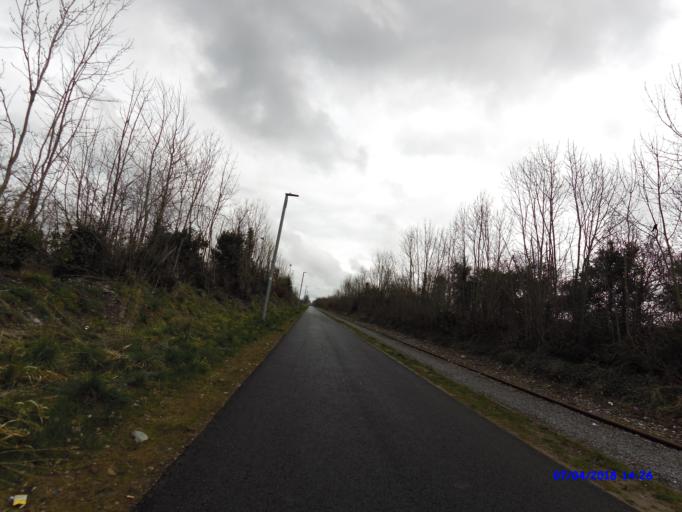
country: IE
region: Leinster
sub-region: An Iarmhi
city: Athlone
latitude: 53.4265
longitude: -7.9228
